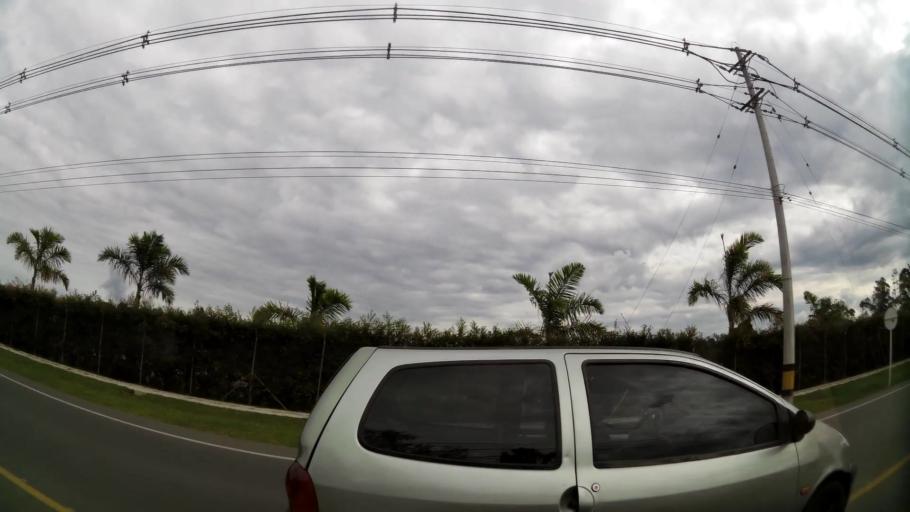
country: CO
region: Antioquia
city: Rionegro
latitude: 6.1458
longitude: -75.4276
